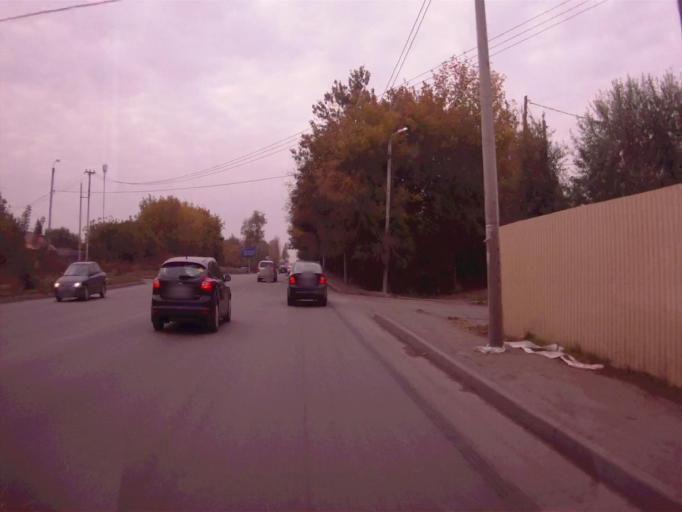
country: RU
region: Chelyabinsk
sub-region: Gorod Chelyabinsk
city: Chelyabinsk
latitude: 55.1287
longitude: 61.3854
